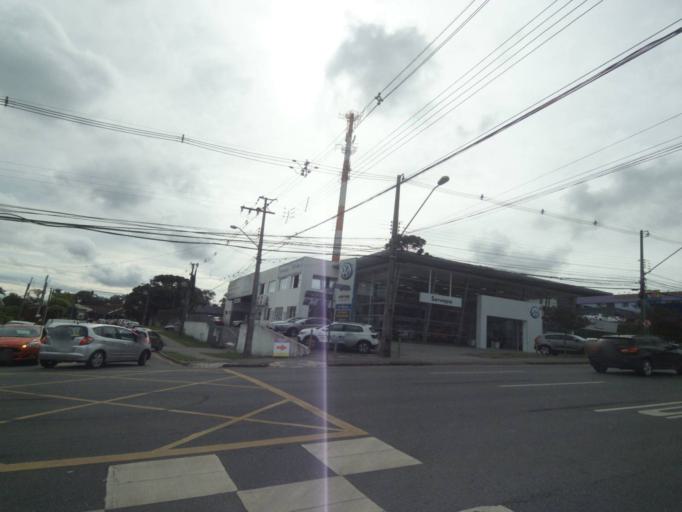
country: BR
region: Parana
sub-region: Curitiba
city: Curitiba
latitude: -25.4416
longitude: -49.3058
